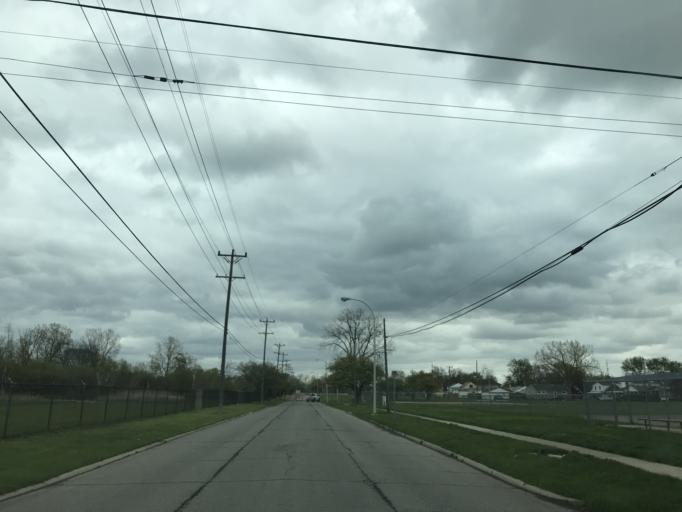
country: US
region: Michigan
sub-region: Wayne County
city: Riverview
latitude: 42.1799
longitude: -83.1764
